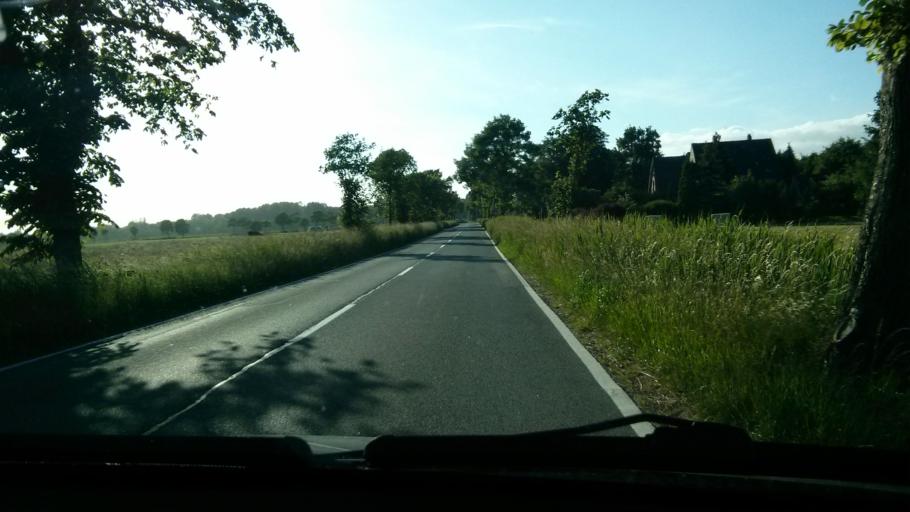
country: DE
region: Bremen
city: Bremerhaven
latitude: 53.4786
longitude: 8.5689
